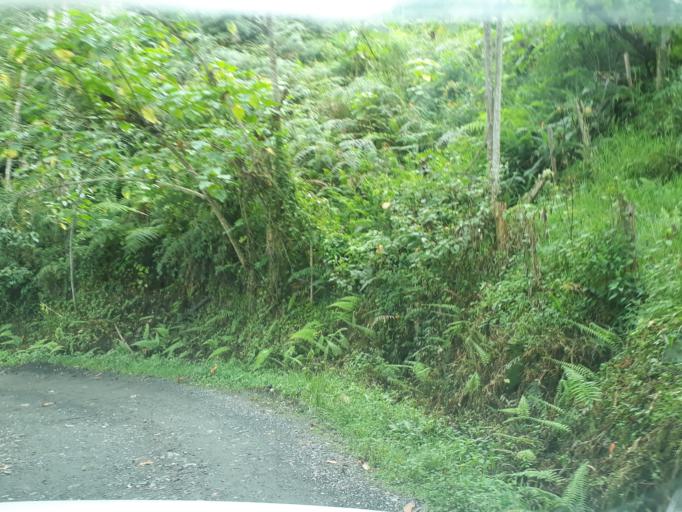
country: CO
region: Cundinamarca
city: Carmen de Carupa
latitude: 5.3544
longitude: -74.0625
